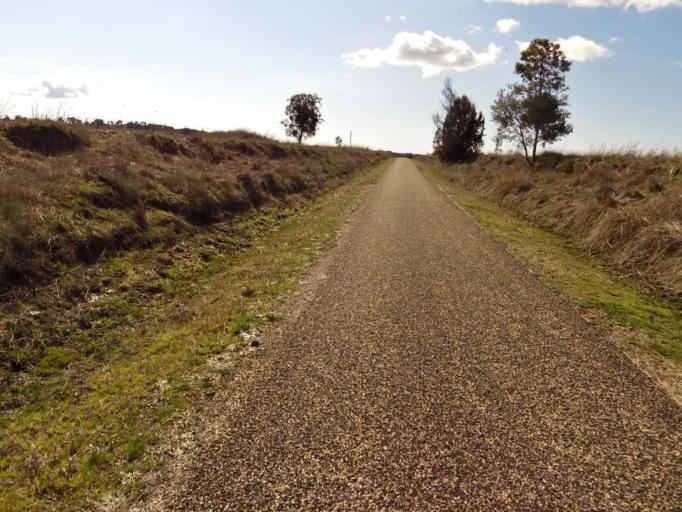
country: AU
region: Victoria
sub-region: Wangaratta
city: Wangaratta
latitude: -36.3981
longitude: 146.6503
